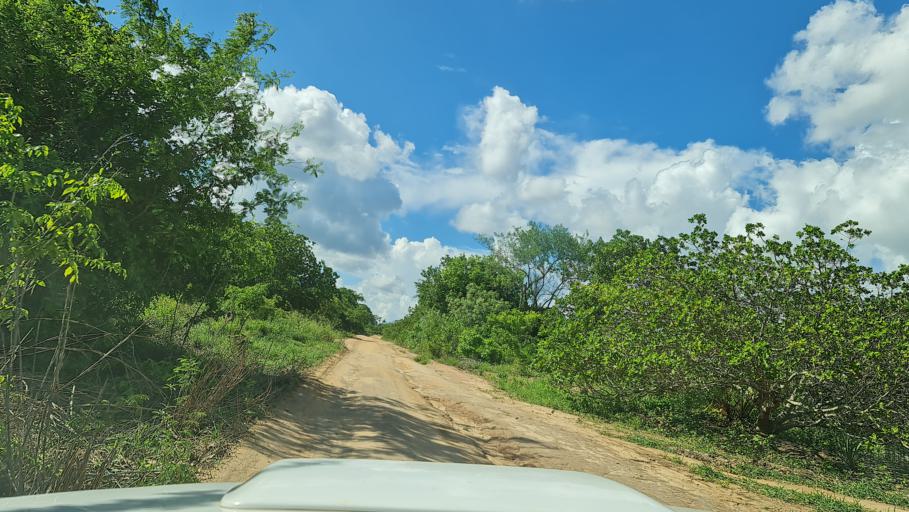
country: MZ
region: Nampula
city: Ilha de Mocambique
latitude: -15.4222
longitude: 40.2675
